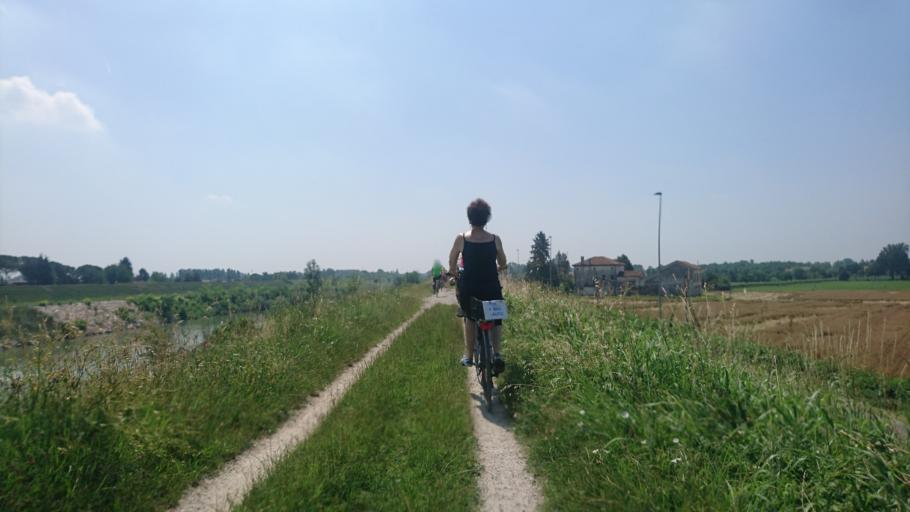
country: IT
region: Veneto
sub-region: Provincia di Padova
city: Oltre Brenta
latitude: 45.4047
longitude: 11.9997
